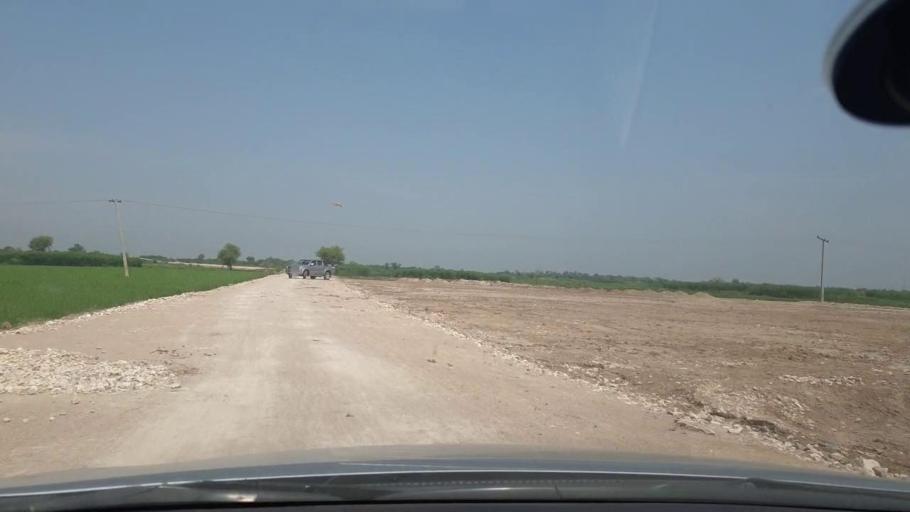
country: PK
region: Balochistan
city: Garhi Khairo
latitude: 28.0563
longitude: 68.0000
